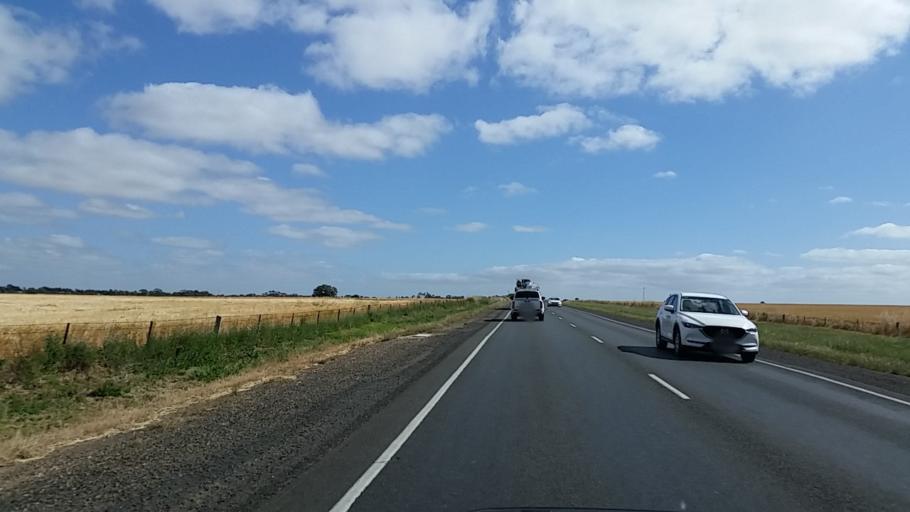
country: AU
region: South Australia
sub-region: Light
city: Roseworthy
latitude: -34.5541
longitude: 138.7480
